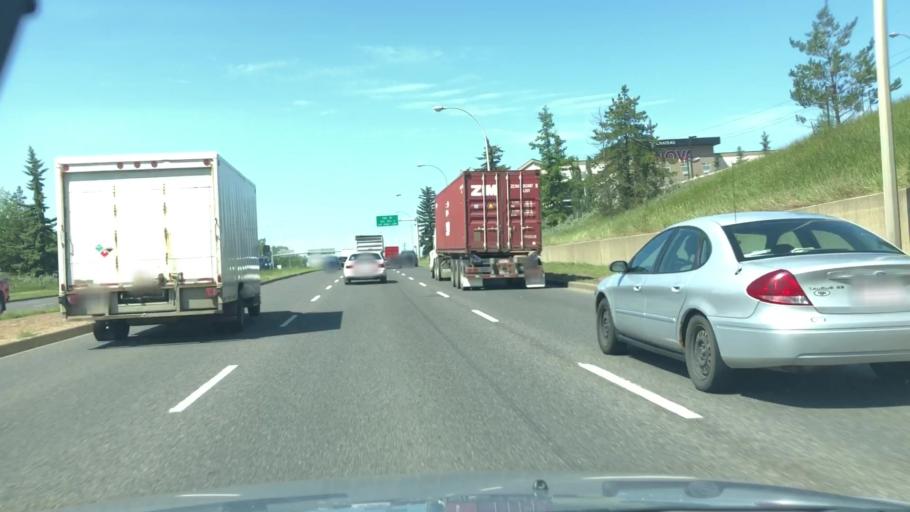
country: CA
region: Alberta
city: St. Albert
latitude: 53.5812
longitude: -113.5577
